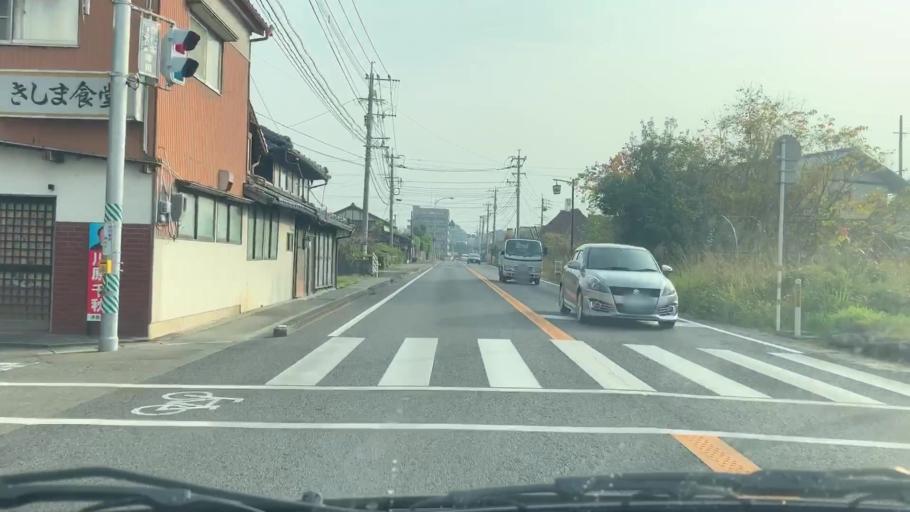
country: JP
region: Saga Prefecture
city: Takeocho-takeo
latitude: 33.2204
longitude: 130.0692
